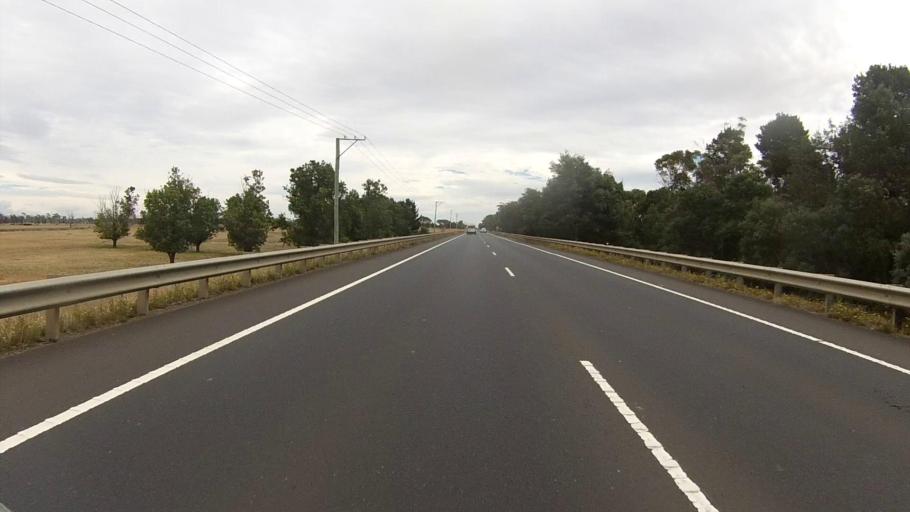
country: AU
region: Tasmania
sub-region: Northern Midlands
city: Evandale
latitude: -41.6920
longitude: 147.2832
